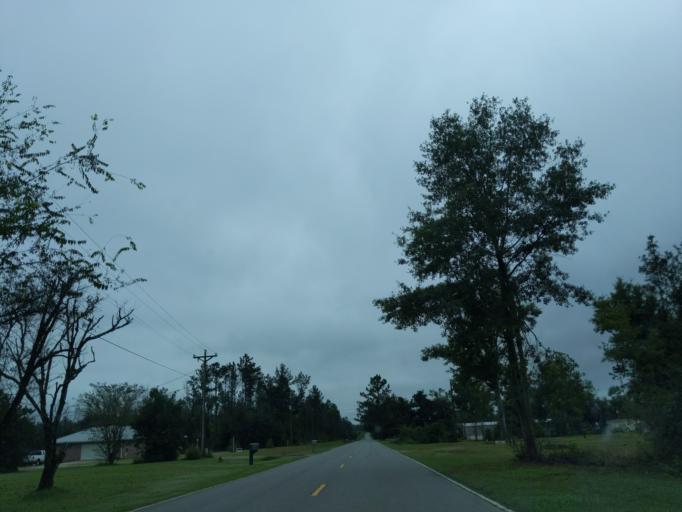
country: US
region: Florida
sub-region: Jackson County
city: Sneads
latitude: 30.7035
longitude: -84.9239
